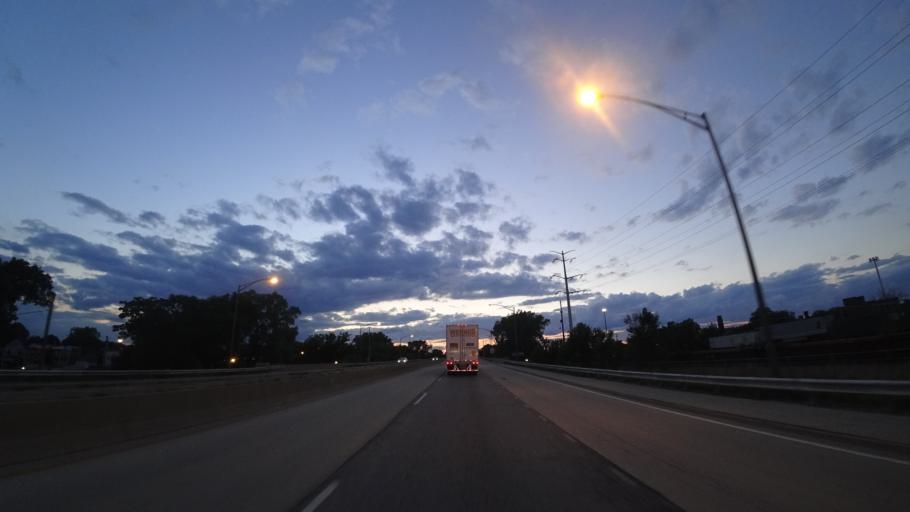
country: US
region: Illinois
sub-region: Cook County
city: Chicago
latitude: 41.7708
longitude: -87.6149
